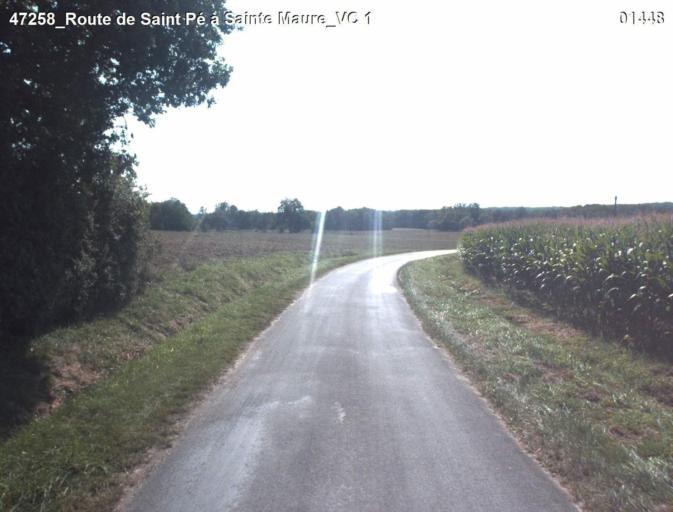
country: FR
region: Midi-Pyrenees
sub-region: Departement du Gers
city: Montreal
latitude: 44.0148
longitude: 0.1392
